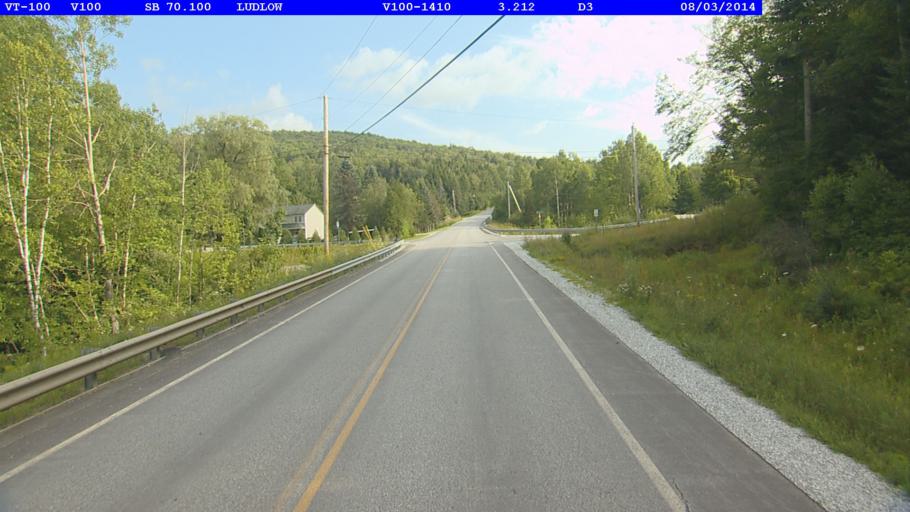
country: US
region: Vermont
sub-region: Windsor County
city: Chester
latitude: 43.3736
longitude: -72.7186
